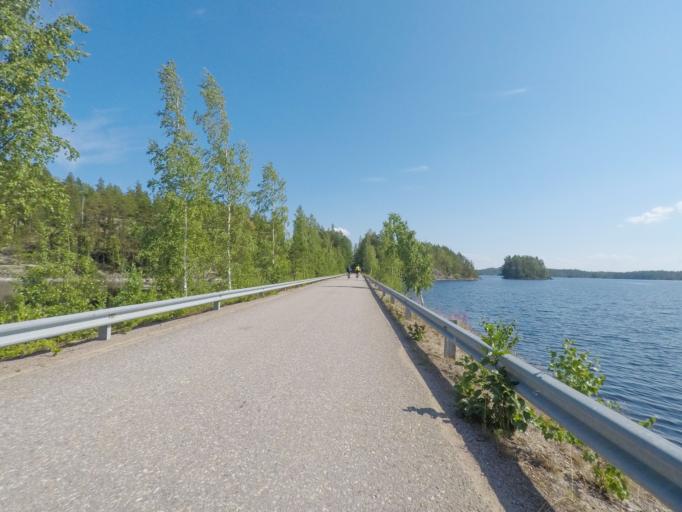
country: FI
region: Southern Savonia
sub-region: Mikkeli
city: Puumala
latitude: 61.4061
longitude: 28.0645
